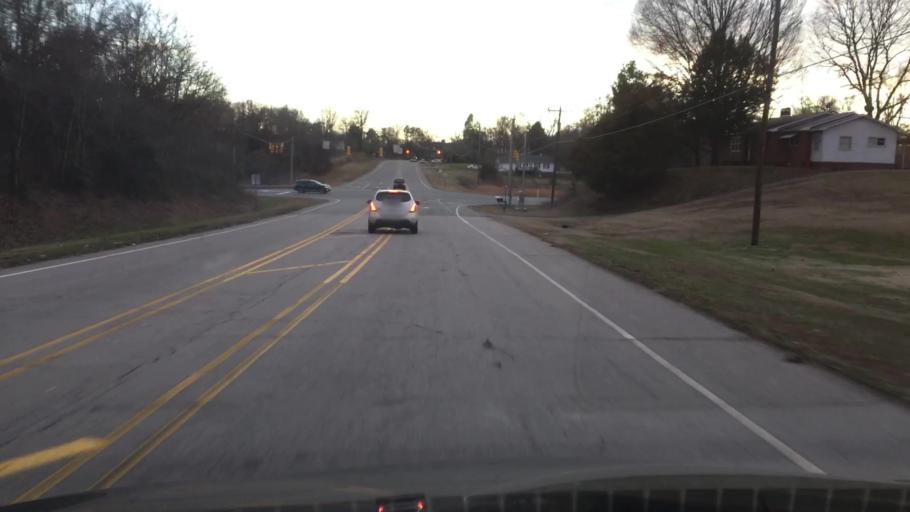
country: US
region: North Carolina
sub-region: Rockingham County
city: Reidsville
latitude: 36.3780
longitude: -79.6565
